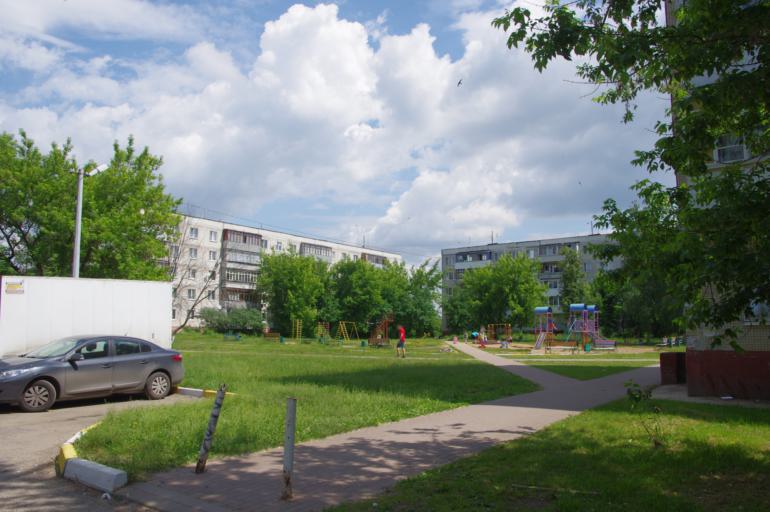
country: RU
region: Moskovskaya
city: Malyshevo
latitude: 55.5413
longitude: 38.3107
